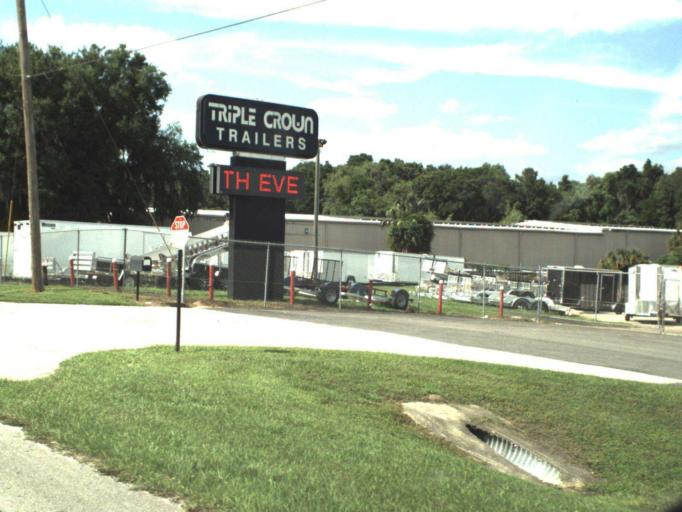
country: US
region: Florida
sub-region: Marion County
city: Ocala
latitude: 29.1456
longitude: -82.1136
